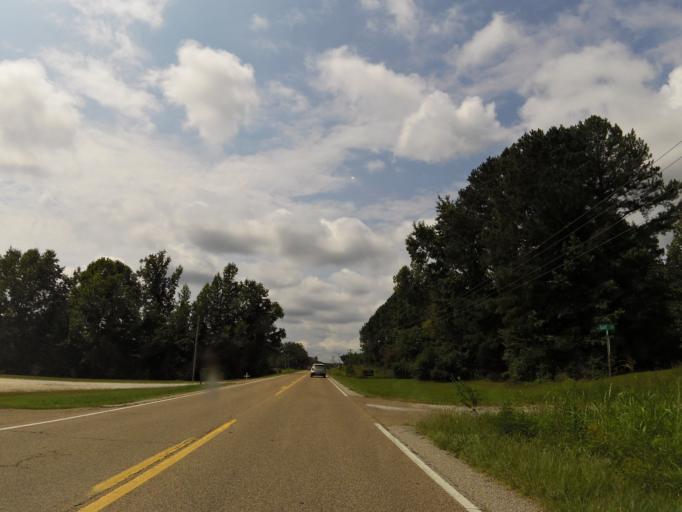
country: US
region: Tennessee
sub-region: Decatur County
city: Decaturville
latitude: 35.5273
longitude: -88.2460
